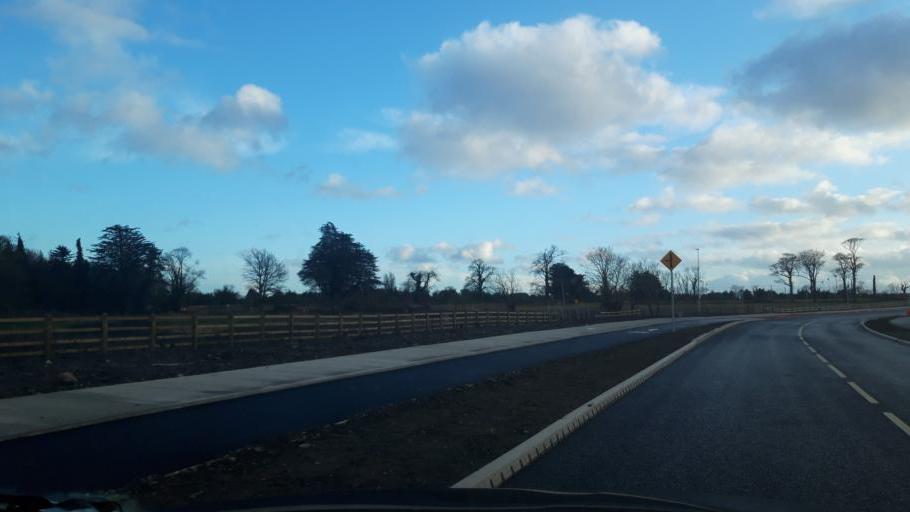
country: IE
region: Leinster
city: Portraine
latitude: 53.4907
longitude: -6.1304
